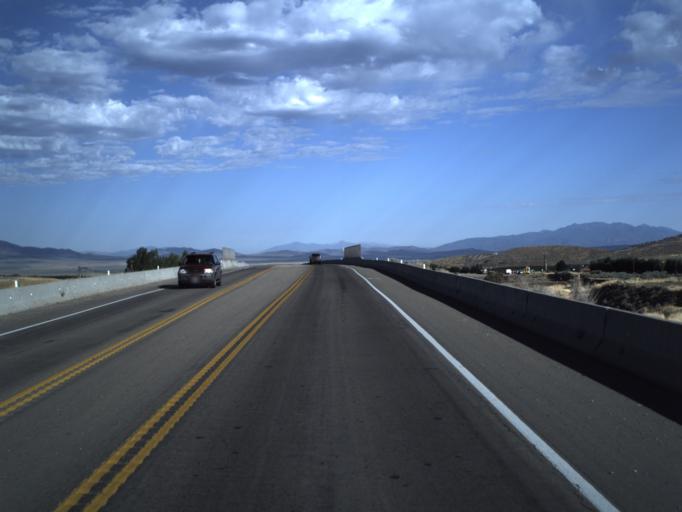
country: US
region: Utah
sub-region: Utah County
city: Santaquin
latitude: 39.9799
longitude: -111.8024
